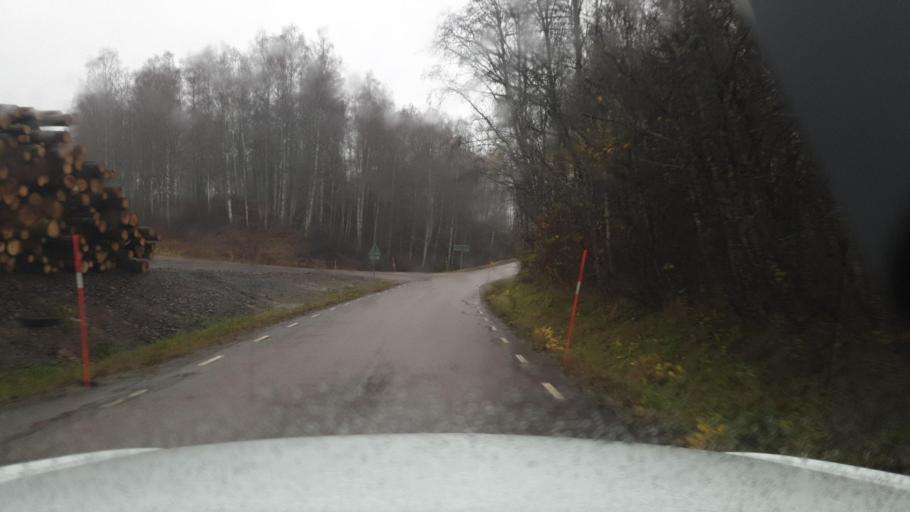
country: SE
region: Vaermland
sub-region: Sunne Kommun
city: Sunne
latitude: 59.7969
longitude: 13.1246
